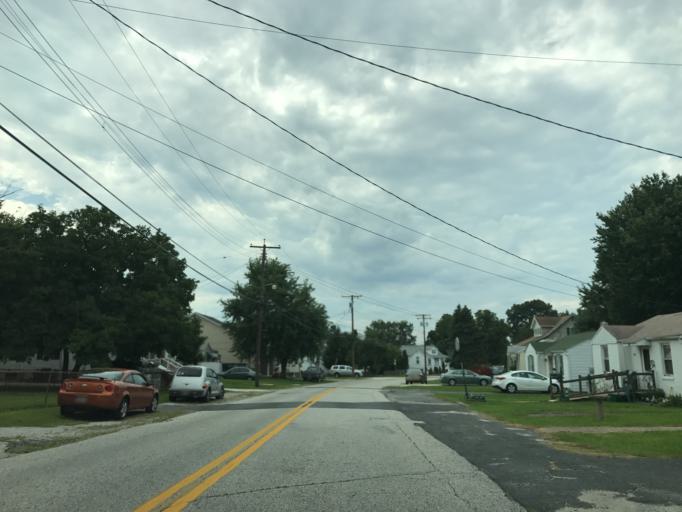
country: US
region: Maryland
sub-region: Baltimore County
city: Essex
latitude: 39.3102
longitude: -76.4830
